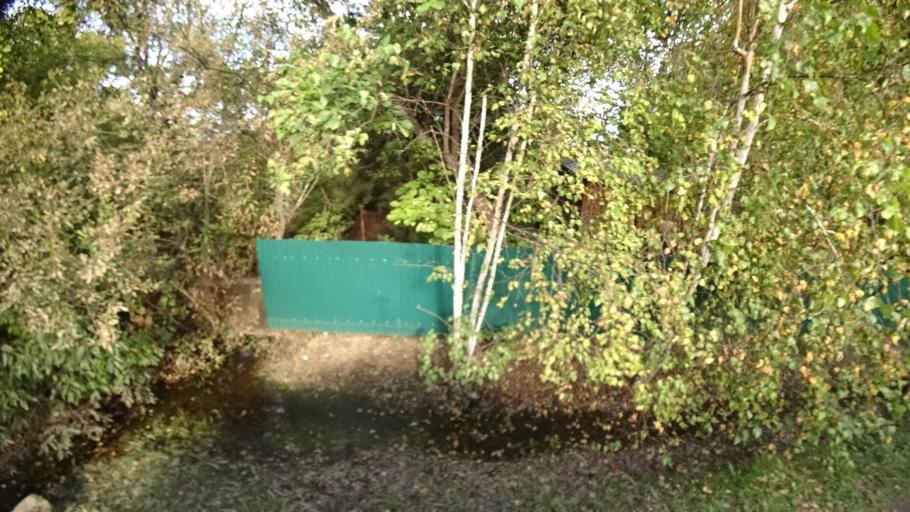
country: RU
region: Primorskiy
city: Dostoyevka
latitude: 44.2936
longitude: 133.4298
